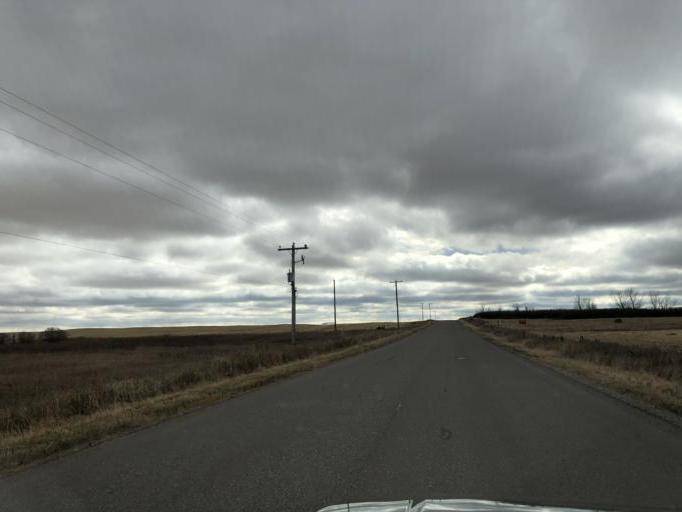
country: CA
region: Alberta
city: Chestermere
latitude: 50.9153
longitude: -113.8830
